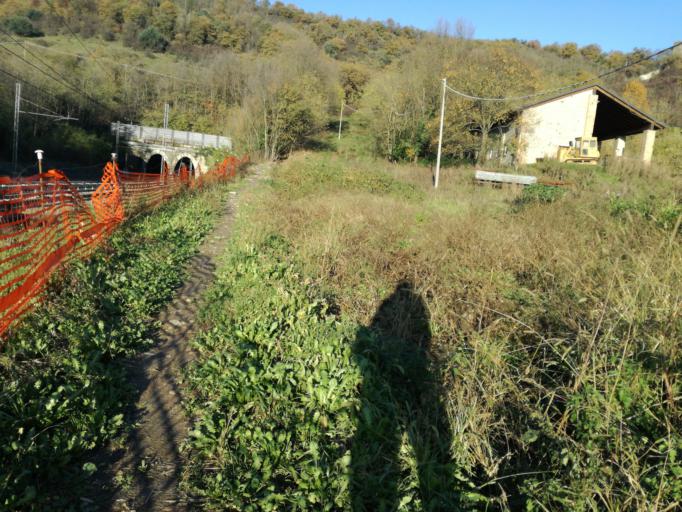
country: IT
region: Veneto
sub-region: Provincia di Padova
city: Battaglia Terme
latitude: 45.3024
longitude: 11.7840
